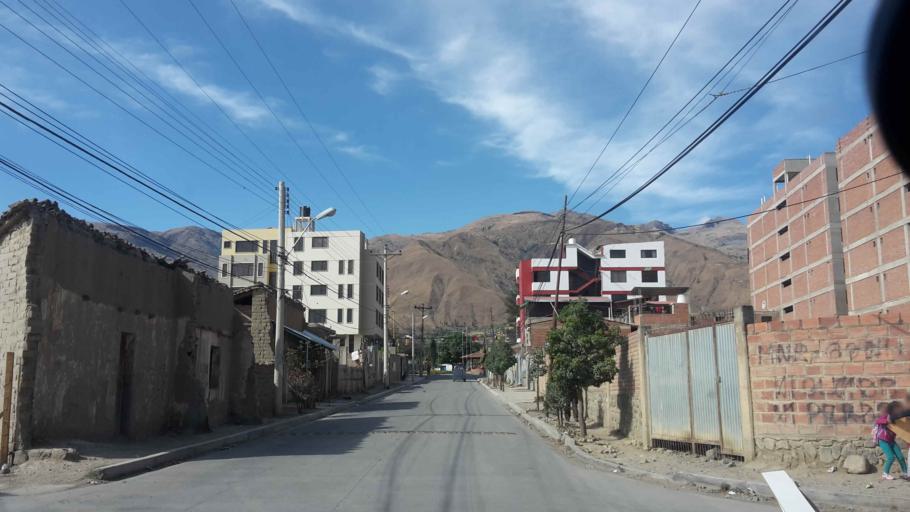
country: BO
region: Cochabamba
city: Cochabamba
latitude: -17.3465
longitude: -66.2046
